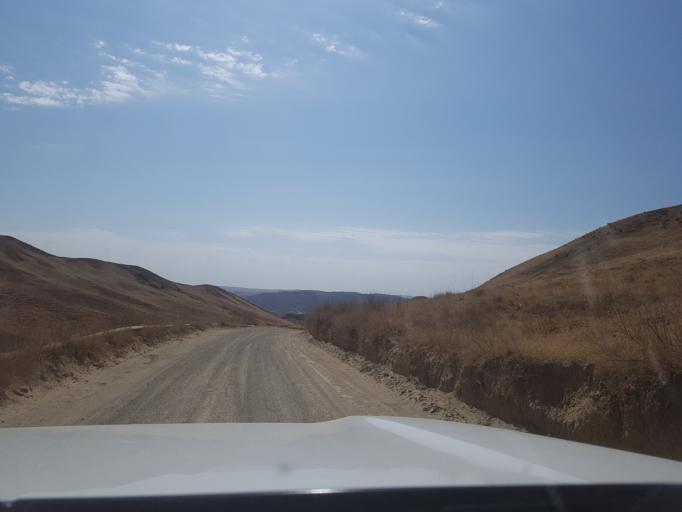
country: TM
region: Ahal
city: Baharly
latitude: 38.2618
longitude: 56.8882
